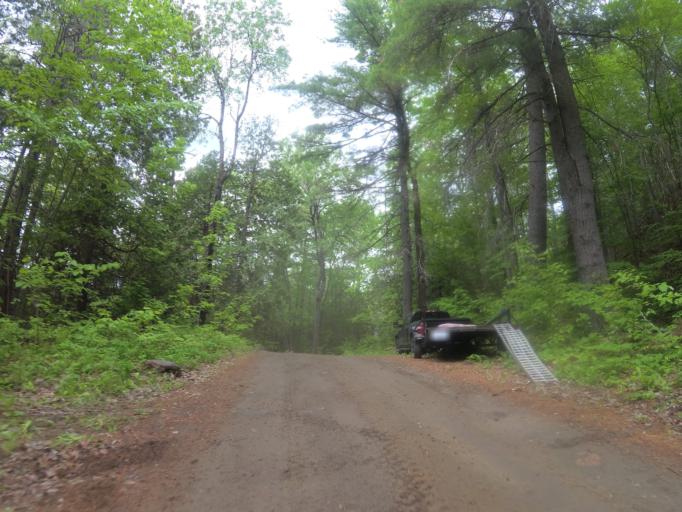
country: CA
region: Ontario
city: Renfrew
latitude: 45.1078
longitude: -76.8238
